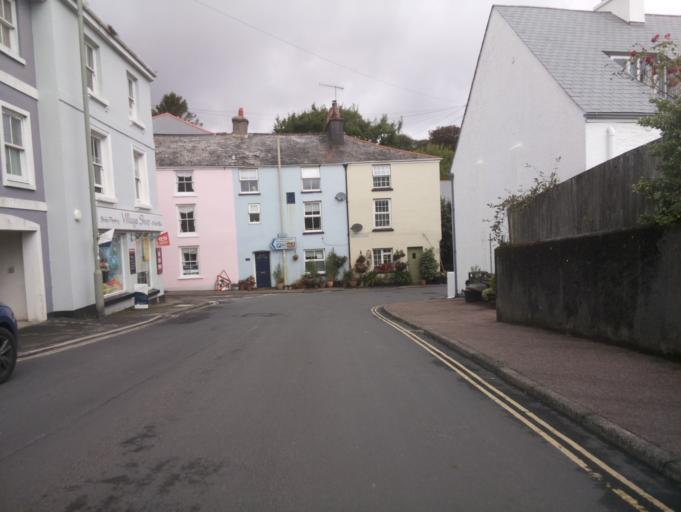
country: GB
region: England
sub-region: Devon
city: Dartmouth
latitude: 50.3243
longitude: -3.5992
